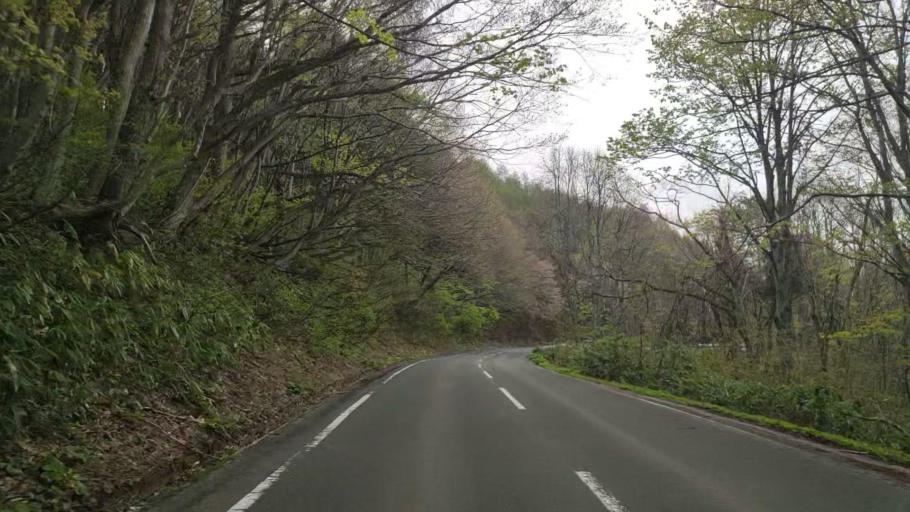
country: JP
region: Aomori
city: Aomori Shi
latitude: 40.7337
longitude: 140.8397
